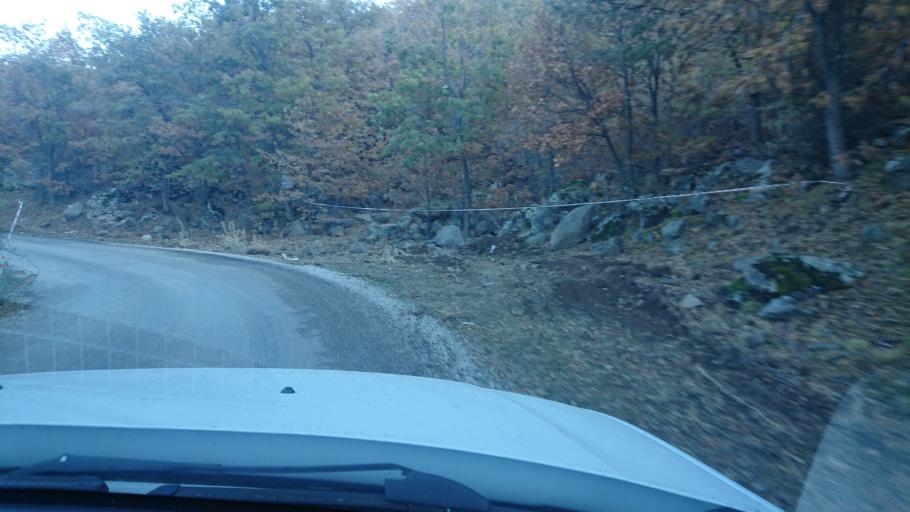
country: TR
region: Aksaray
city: Taspinar
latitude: 38.1652
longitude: 34.2007
